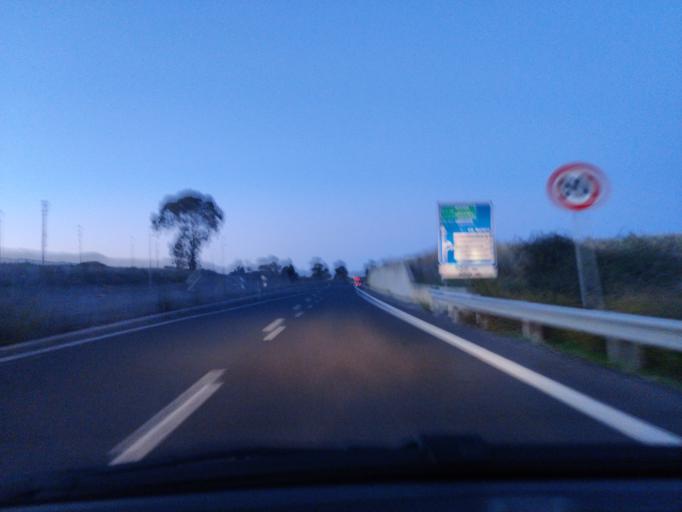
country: IT
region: Latium
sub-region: Citta metropolitana di Roma Capitale
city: Aurelia
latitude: 42.1231
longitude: 11.7913
